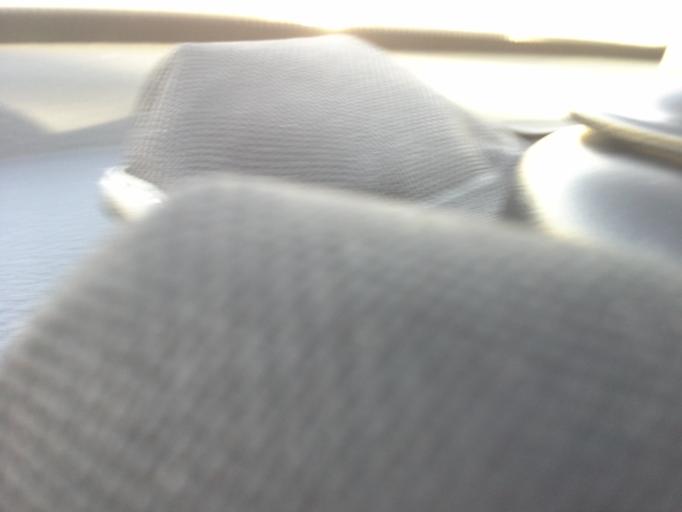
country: TM
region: Ahal
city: Ashgabat
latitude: 37.9626
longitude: 58.4153
